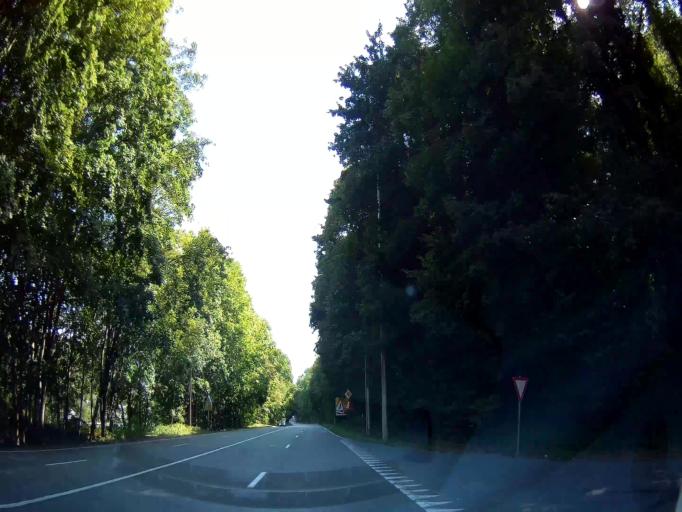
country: BE
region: Wallonia
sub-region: Province de Namur
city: Yvoir
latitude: 50.3234
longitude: 4.8728
